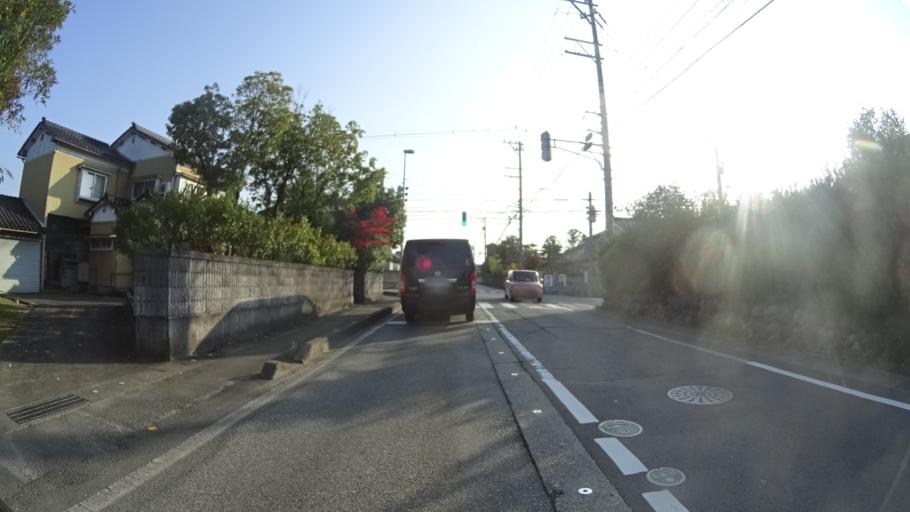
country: JP
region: Toyama
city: Toyama-shi
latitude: 36.6889
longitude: 137.2711
